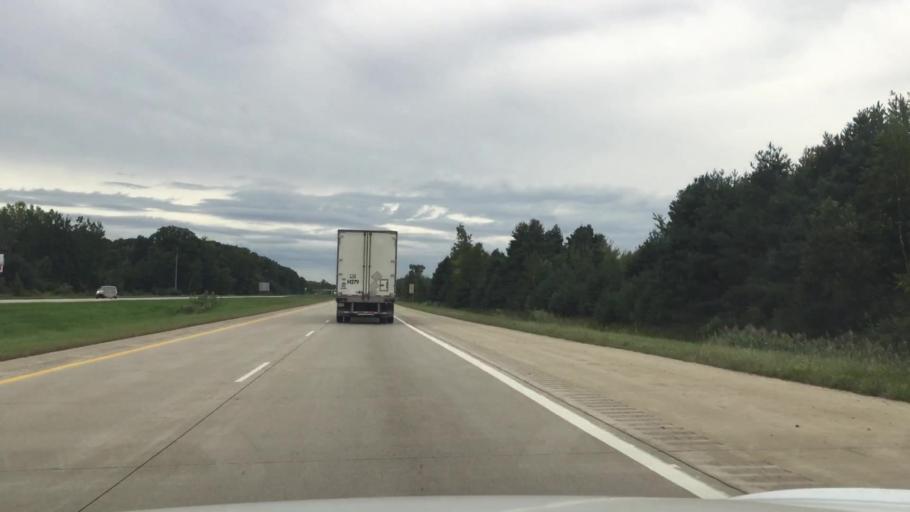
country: US
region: Michigan
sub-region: Saint Clair County
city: Marysville
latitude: 42.9455
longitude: -82.5076
